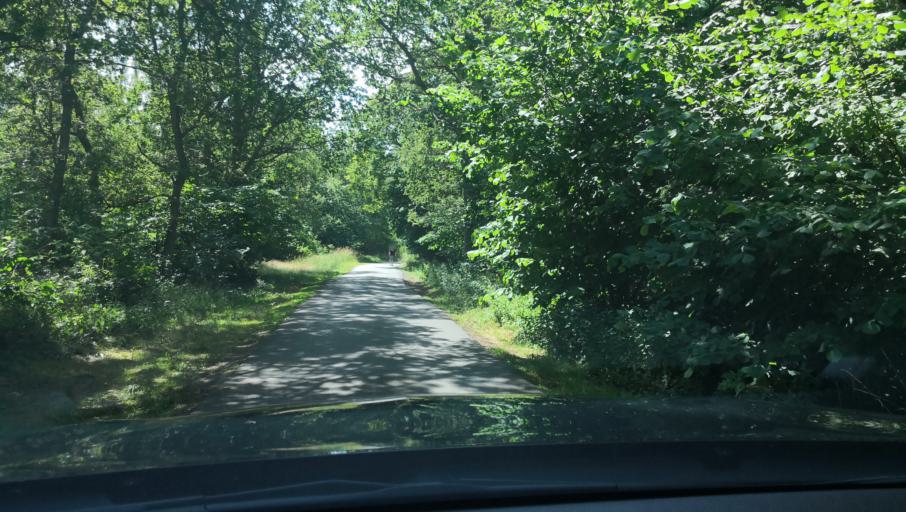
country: SE
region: Skane
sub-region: Ystads Kommun
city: Kopingebro
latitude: 55.3837
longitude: 14.1460
